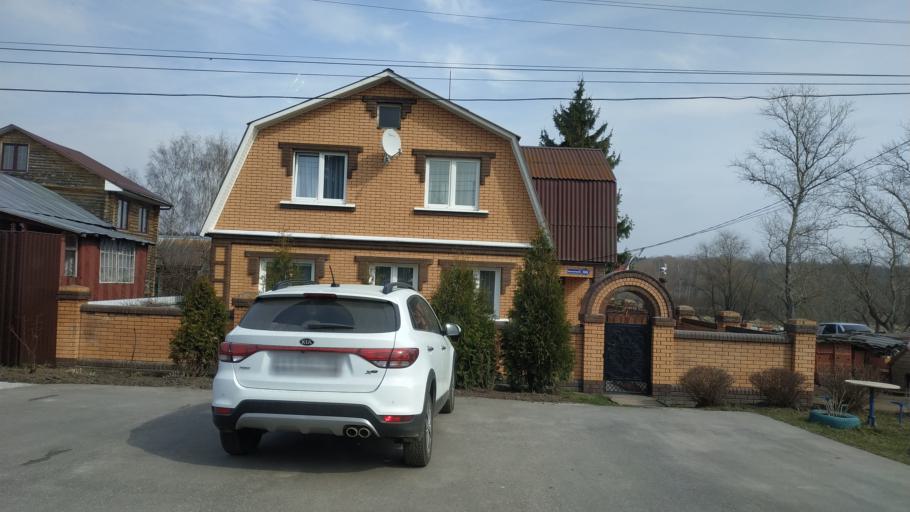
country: RU
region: Moskovskaya
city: Voskresensk
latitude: 55.3399
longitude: 38.6218
